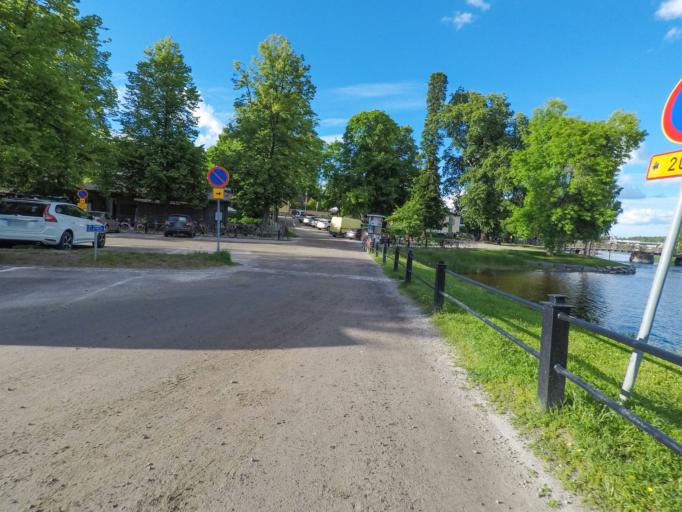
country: FI
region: Southern Savonia
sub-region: Savonlinna
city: Savonlinna
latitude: 61.8642
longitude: 28.8959
